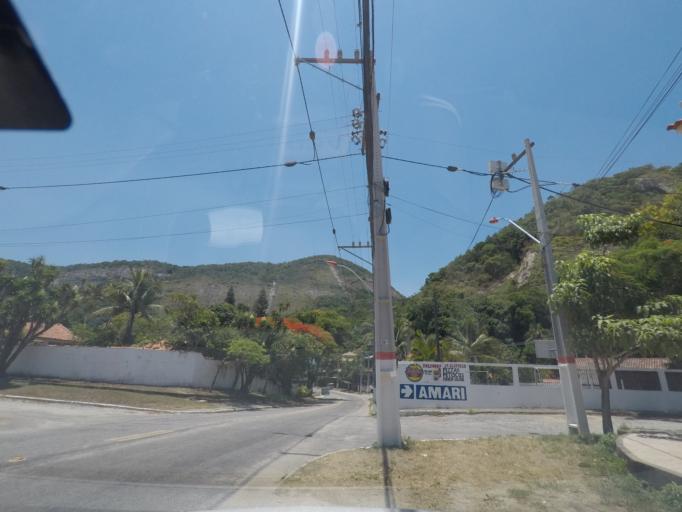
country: BR
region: Rio de Janeiro
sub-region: Niteroi
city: Niteroi
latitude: -22.9656
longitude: -43.0107
